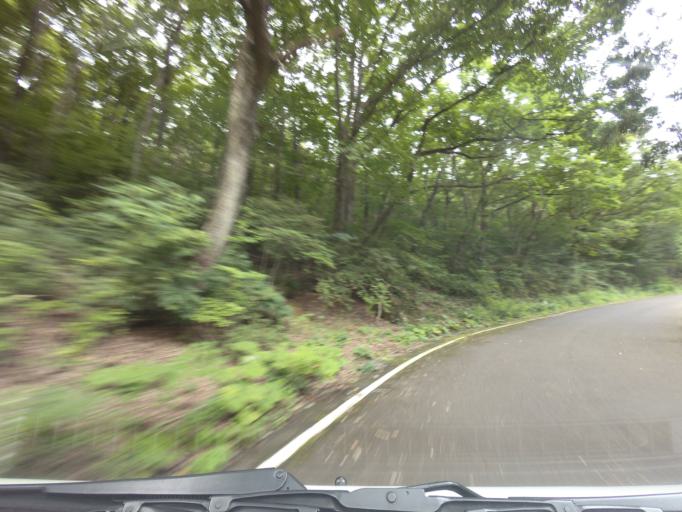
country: JP
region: Fukushima
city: Nihommatsu
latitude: 37.5884
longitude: 140.3362
